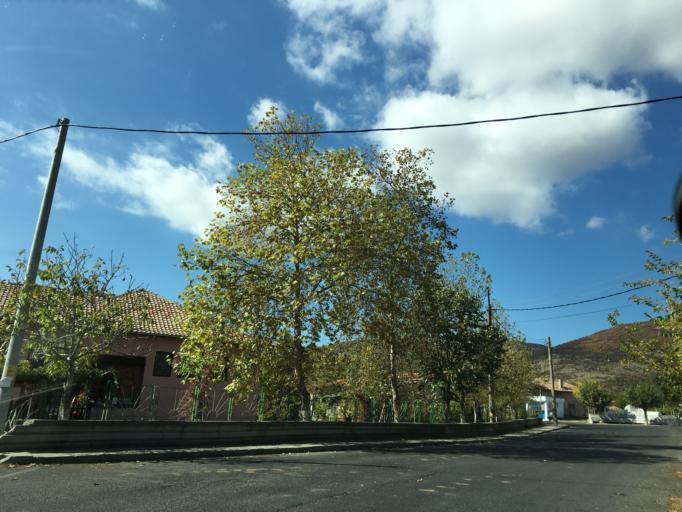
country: BG
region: Kurdzhali
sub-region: Obshtina Kurdzhali
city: Kurdzhali
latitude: 41.5446
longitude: 25.4929
